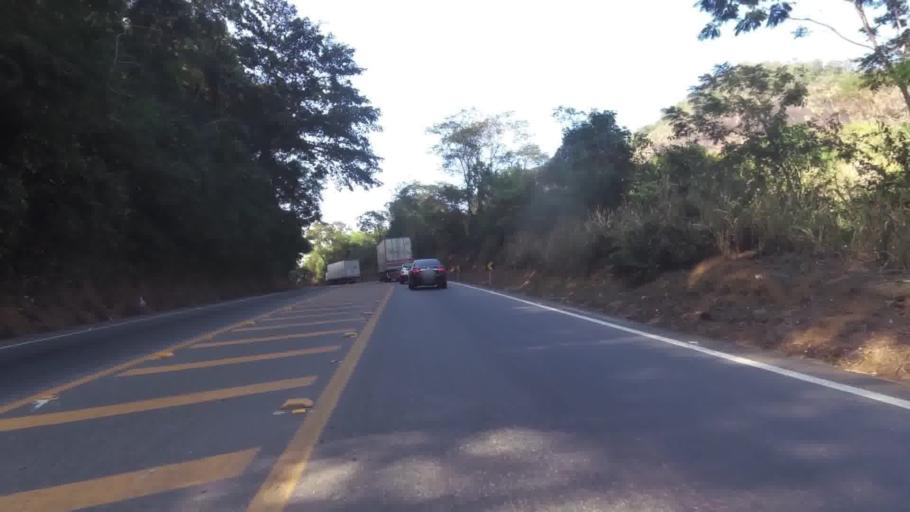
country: BR
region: Espirito Santo
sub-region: Alfredo Chaves
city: Alfredo Chaves
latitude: -20.7095
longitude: -40.7189
